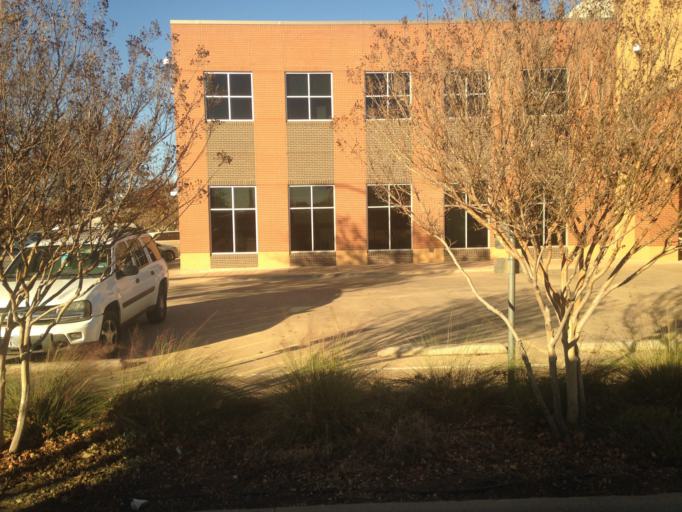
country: US
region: Texas
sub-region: Taylor County
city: Abilene
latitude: 32.4547
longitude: -99.7310
